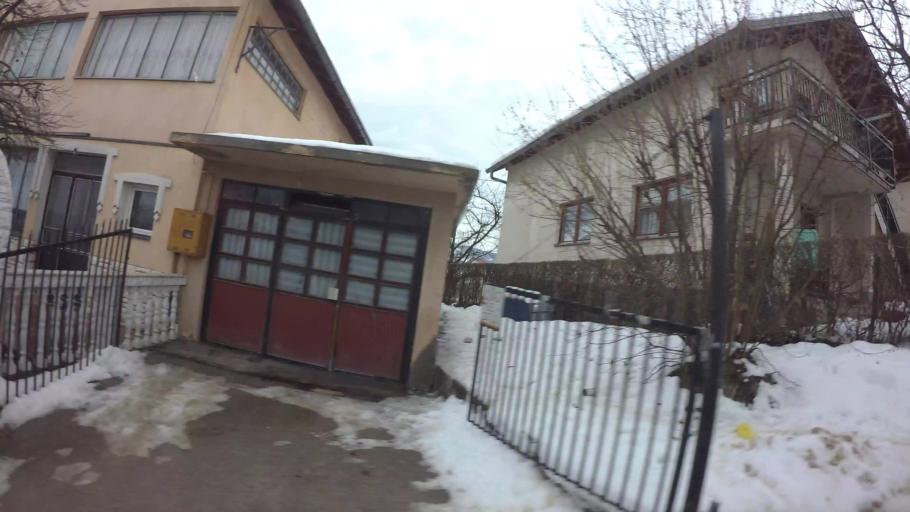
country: BA
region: Federation of Bosnia and Herzegovina
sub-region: Kanton Sarajevo
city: Sarajevo
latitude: 43.8665
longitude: 18.3229
